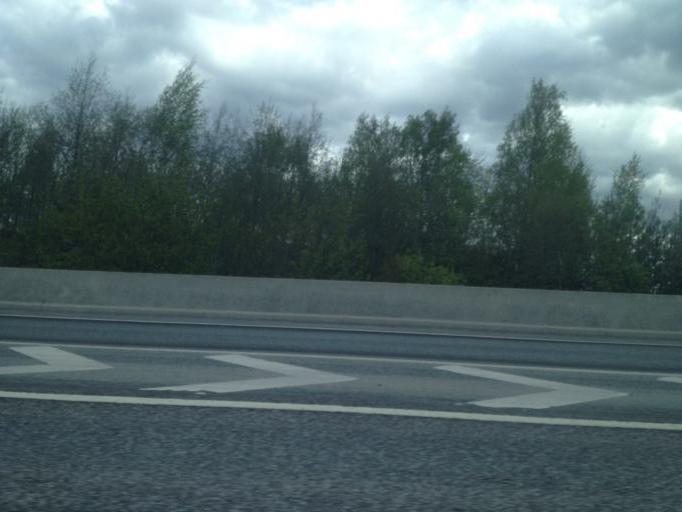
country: FI
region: Haeme
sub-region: Haemeenlinna
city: Haemeenlinna
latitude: 60.9660
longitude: 24.4781
